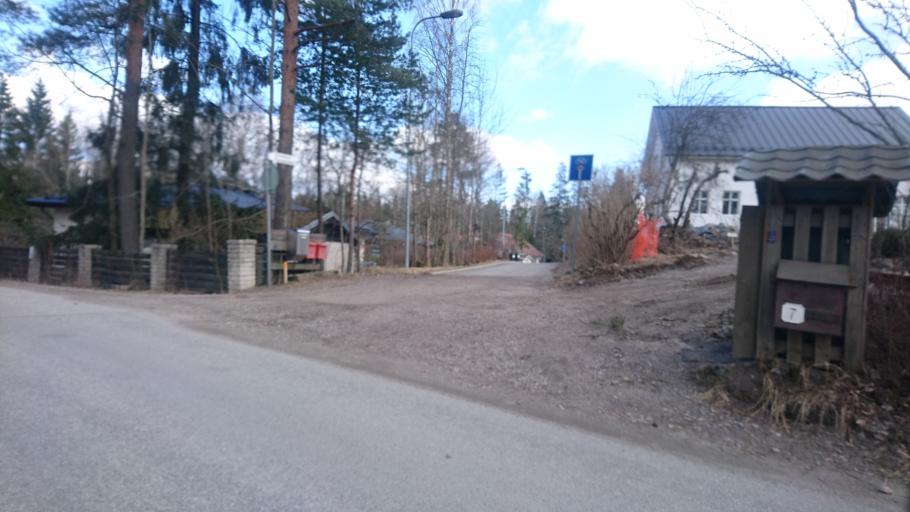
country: FI
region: Uusimaa
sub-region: Helsinki
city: Kauniainen
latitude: 60.1993
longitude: 24.7164
